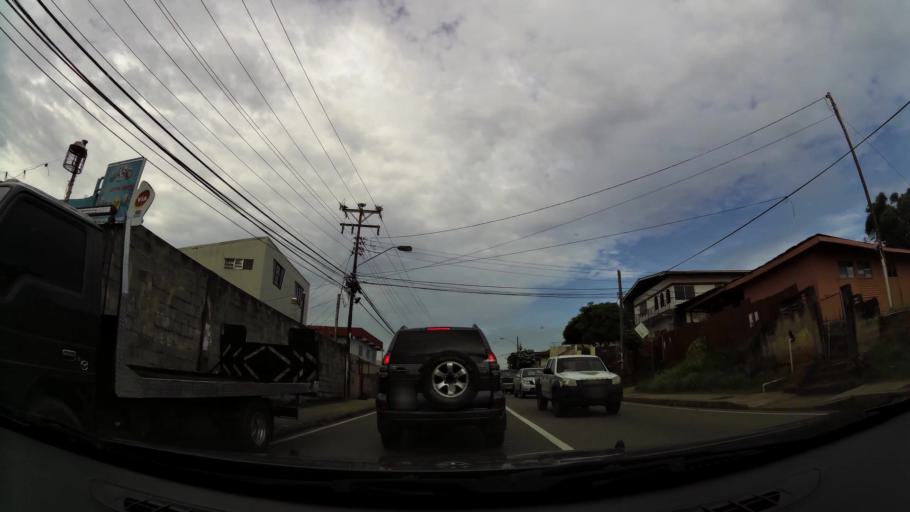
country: TT
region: Tunapuna/Piarco
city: Tunapuna
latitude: 10.6512
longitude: -61.4389
